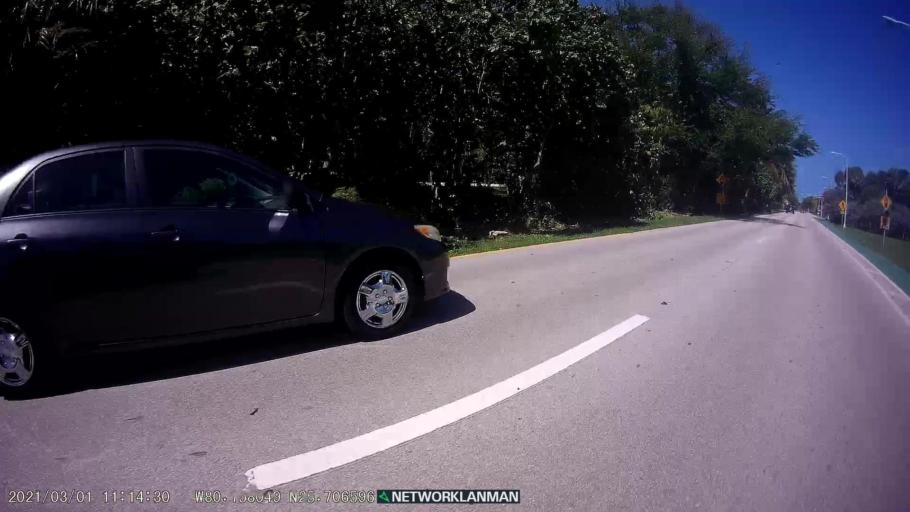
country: US
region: Florida
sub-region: Miami-Dade County
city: Key Biscayne
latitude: 25.7069
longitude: -80.1576
